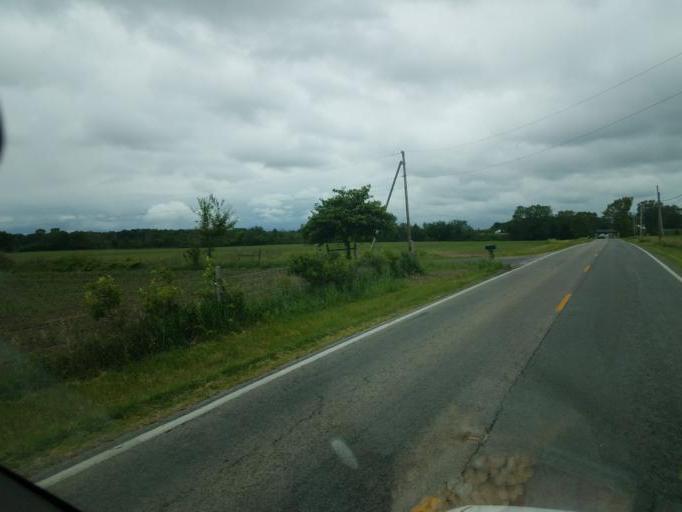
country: US
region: Ohio
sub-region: Marion County
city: Marion
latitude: 40.5495
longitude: -83.0696
